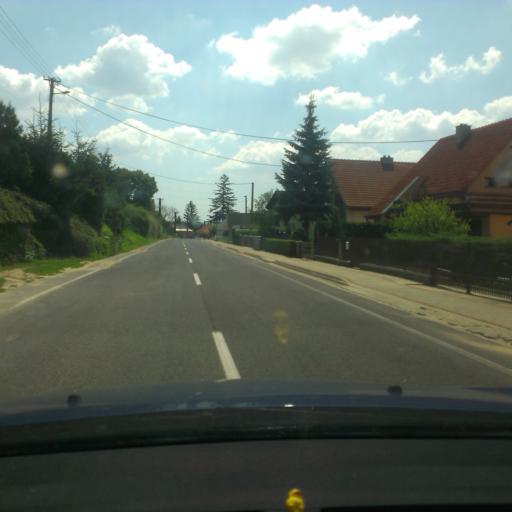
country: SK
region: Trnavsky
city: Hlohovec
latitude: 48.4777
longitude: 17.8079
